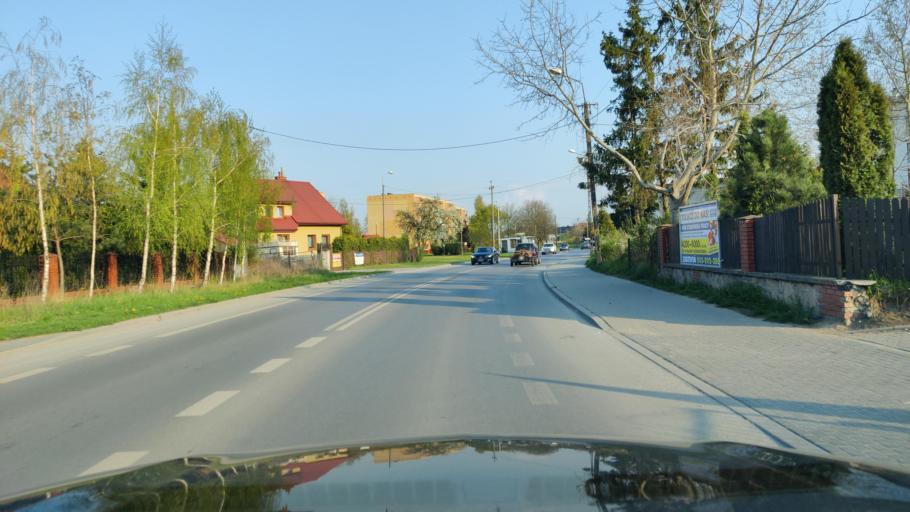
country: PL
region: Masovian Voivodeship
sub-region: Powiat pultuski
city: Pultusk
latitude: 52.6983
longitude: 21.0796
